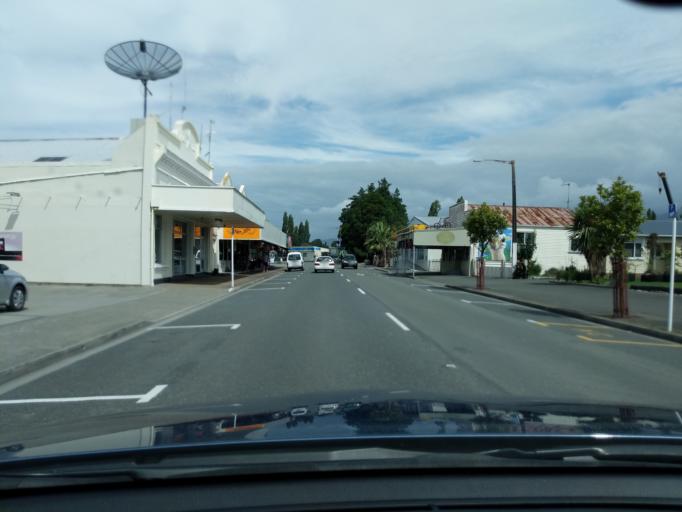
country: NZ
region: Tasman
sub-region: Tasman District
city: Takaka
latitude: -40.8599
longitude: 172.8060
